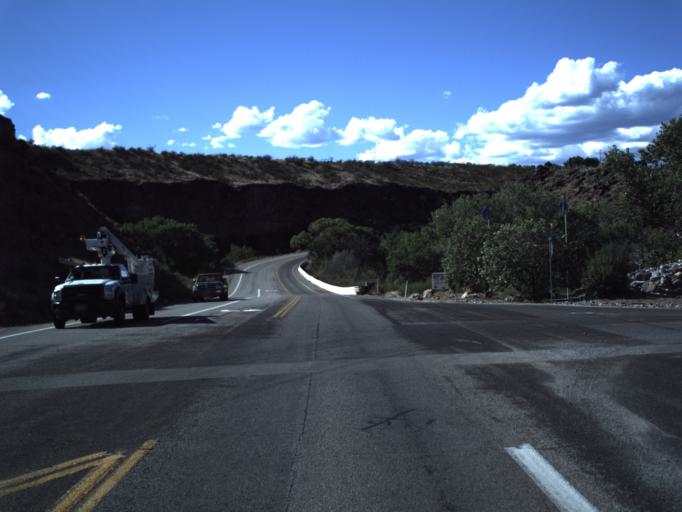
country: US
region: Utah
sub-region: Washington County
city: LaVerkin
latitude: 37.2230
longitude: -113.2796
